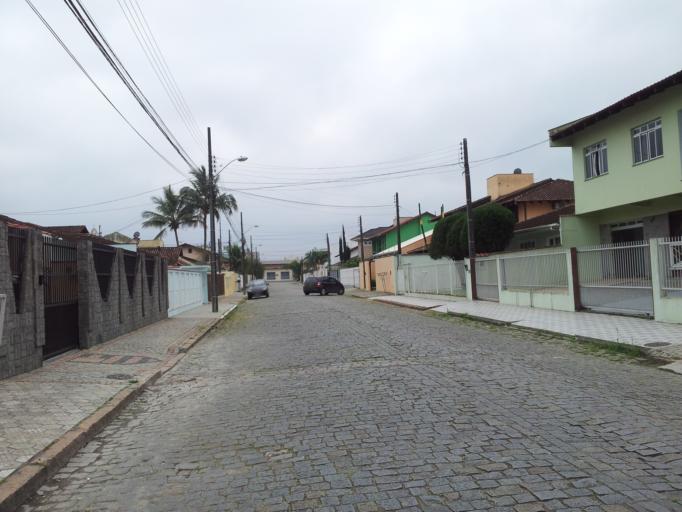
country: BR
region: Santa Catarina
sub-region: Joinville
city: Joinville
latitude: -26.3205
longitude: -48.8411
